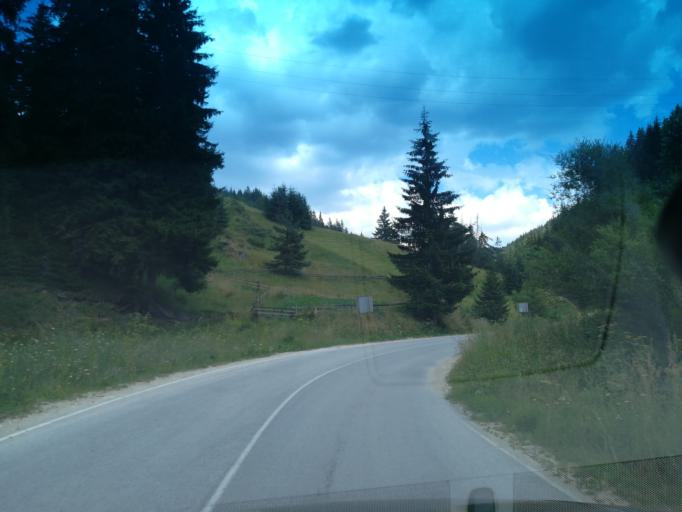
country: BG
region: Smolyan
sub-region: Obshtina Chepelare
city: Chepelare
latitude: 41.6625
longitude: 24.6405
